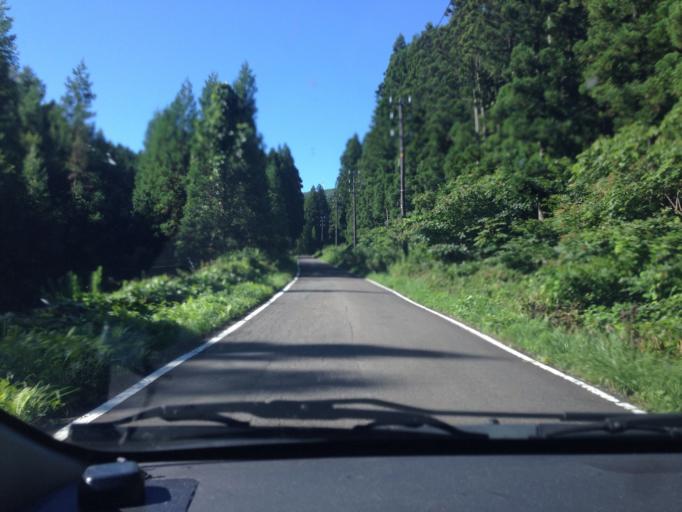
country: JP
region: Fukushima
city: Inawashiro
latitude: 37.3684
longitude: 140.0592
